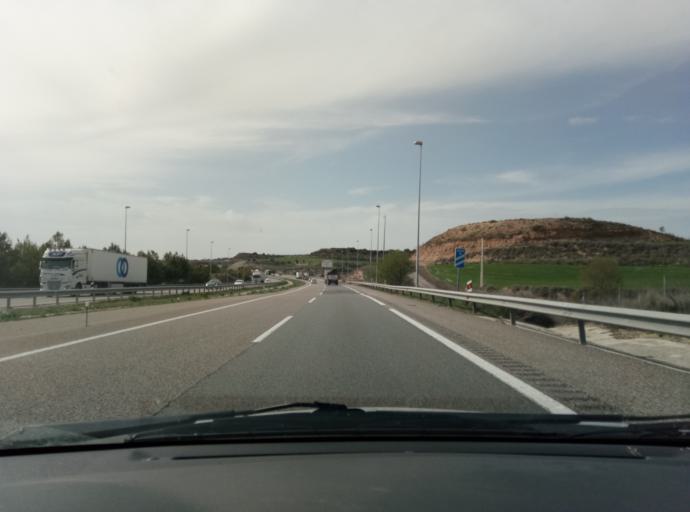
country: ES
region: Catalonia
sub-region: Provincia de Lleida
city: Cervera
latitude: 41.6635
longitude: 1.3047
